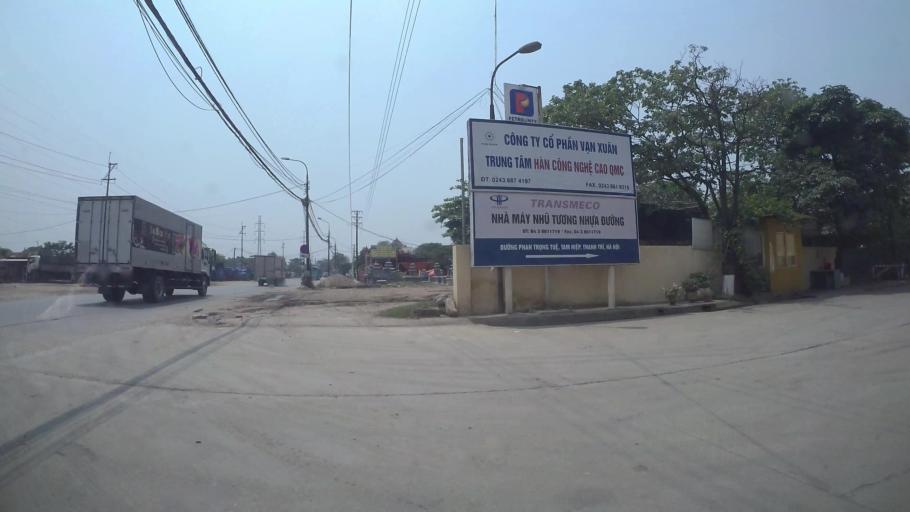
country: VN
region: Ha Noi
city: Van Dien
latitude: 20.9440
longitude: 105.8383
